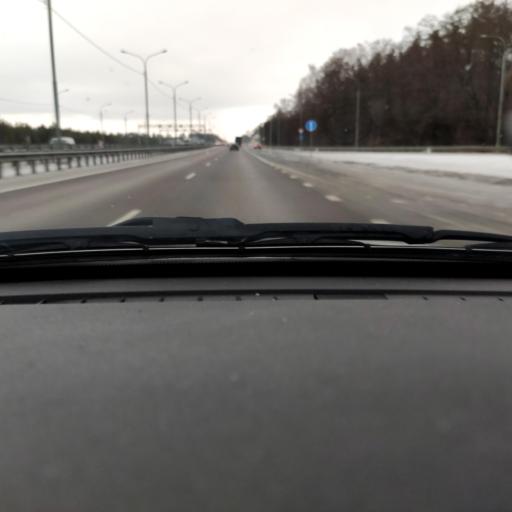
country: RU
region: Voronezj
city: Ramon'
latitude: 51.8922
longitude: 39.2182
